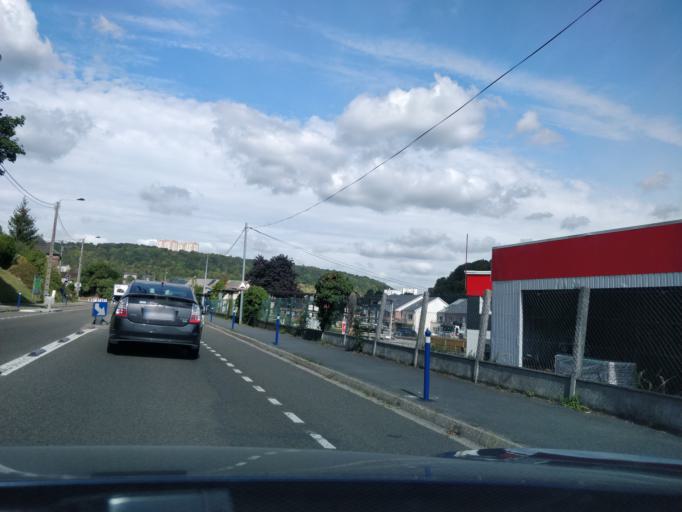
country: FR
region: Haute-Normandie
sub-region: Departement de la Seine-Maritime
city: Saint-Leger-du-Bourg-Denis
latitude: 49.4343
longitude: 1.1512
